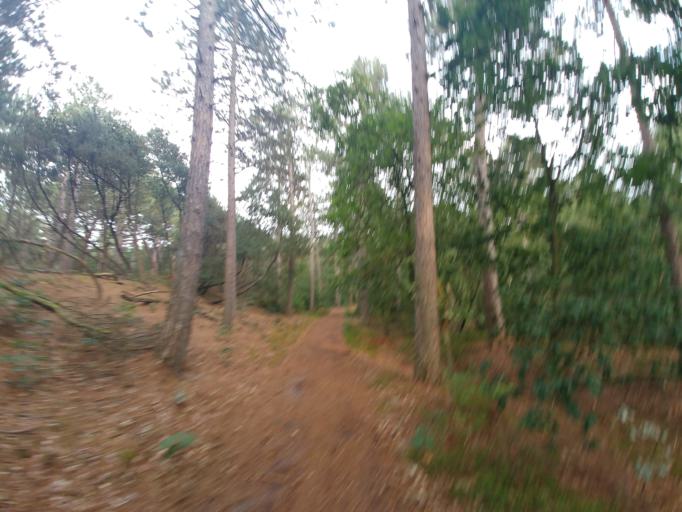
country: NL
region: North Holland
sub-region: Gemeente Heiloo
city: Heiloo
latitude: 52.6871
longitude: 4.6815
